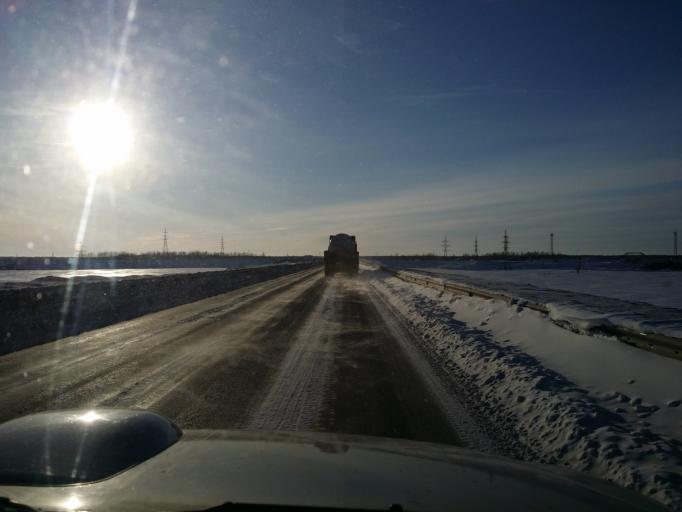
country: RU
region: Khanty-Mansiyskiy Avtonomnyy Okrug
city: Izluchinsk
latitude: 60.9362
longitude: 76.9198
